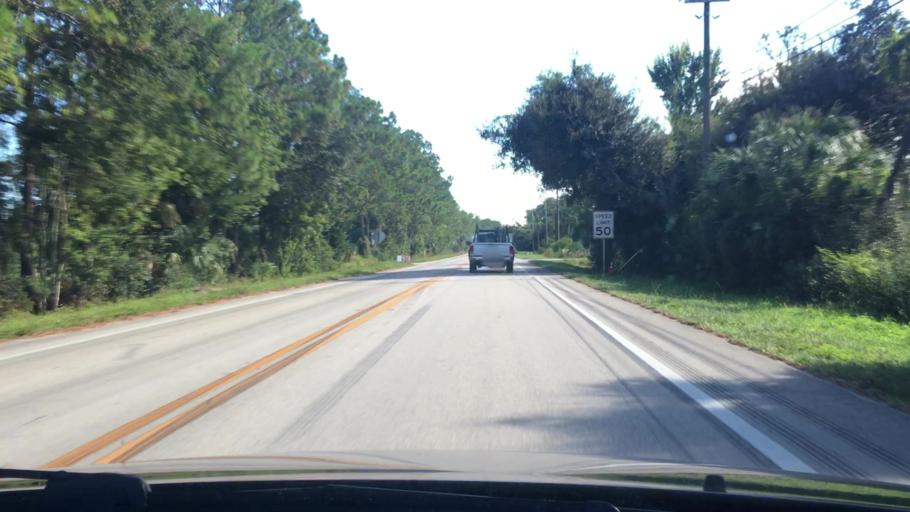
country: US
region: Florida
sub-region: Volusia County
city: Samsula-Spruce Creek
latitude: 29.1051
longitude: -81.0689
